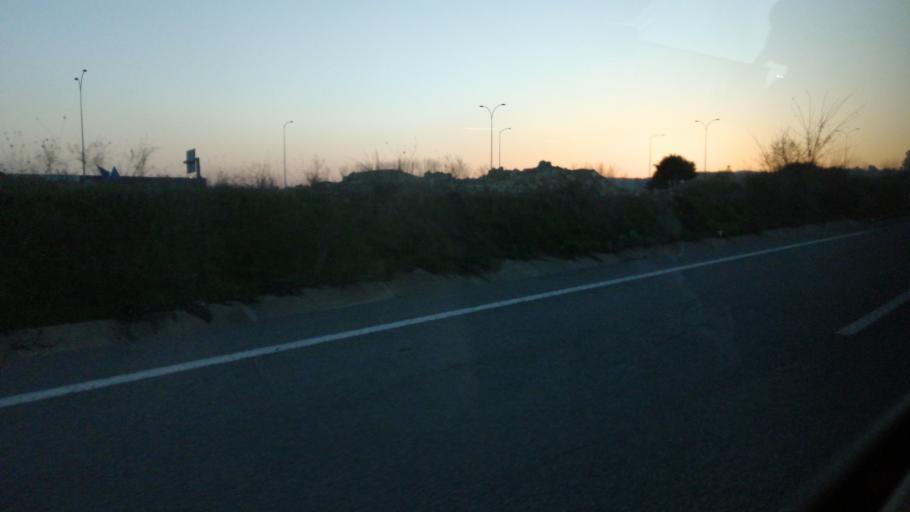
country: TR
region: Kocaeli
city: Tavsanli
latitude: 40.8006
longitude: 29.5061
